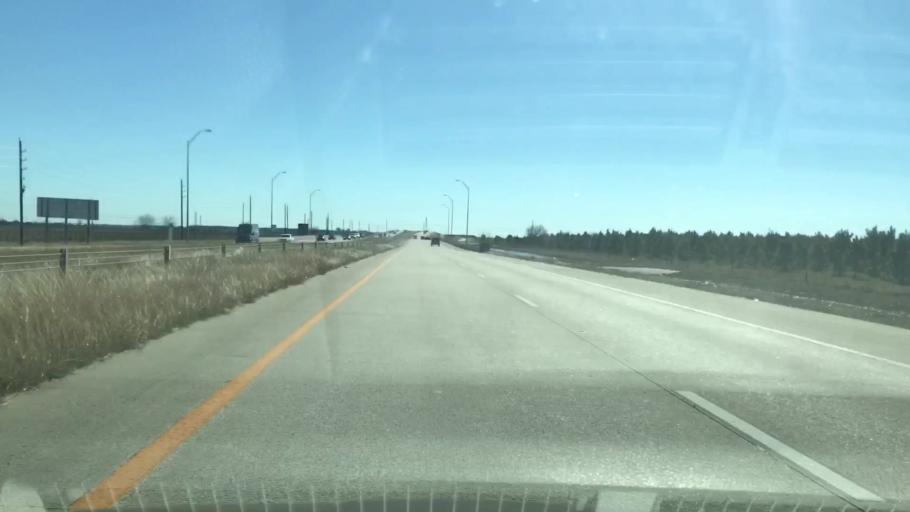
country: US
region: Texas
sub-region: Harris County
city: Cypress
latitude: 29.9298
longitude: -95.7631
